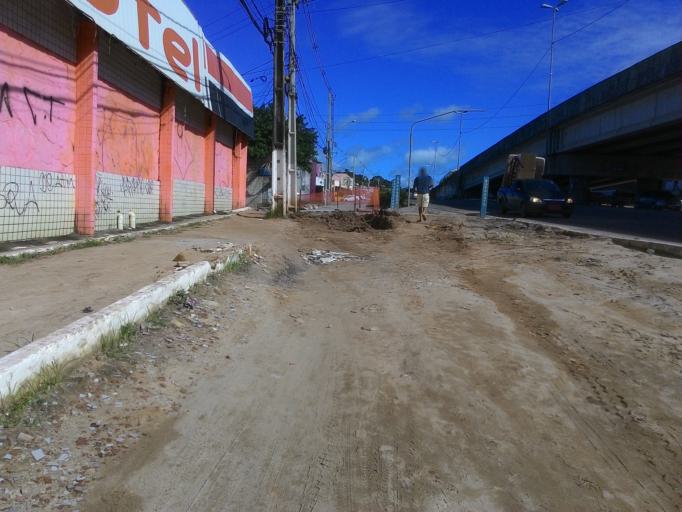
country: BR
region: Pernambuco
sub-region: Olinda
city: Olinda
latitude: -7.9912
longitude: -34.8550
